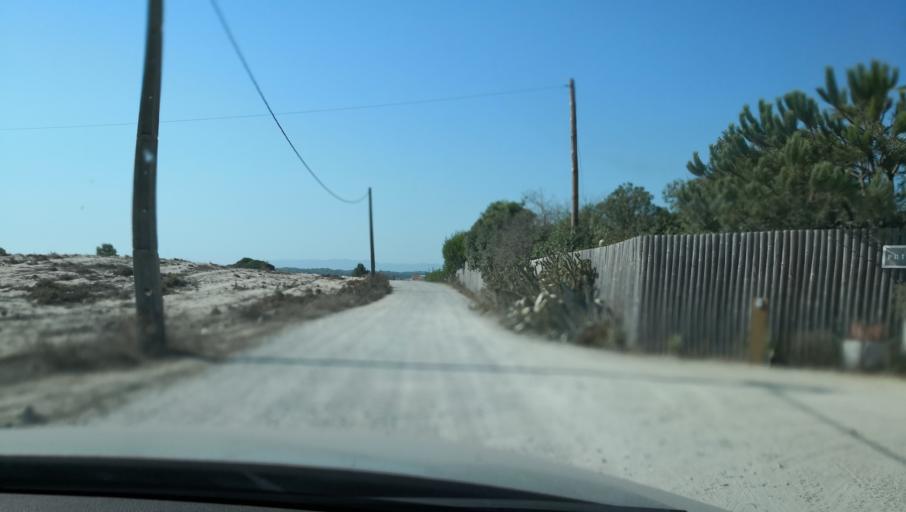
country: PT
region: Setubal
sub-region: Setubal
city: Setubal
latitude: 38.3969
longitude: -8.7843
